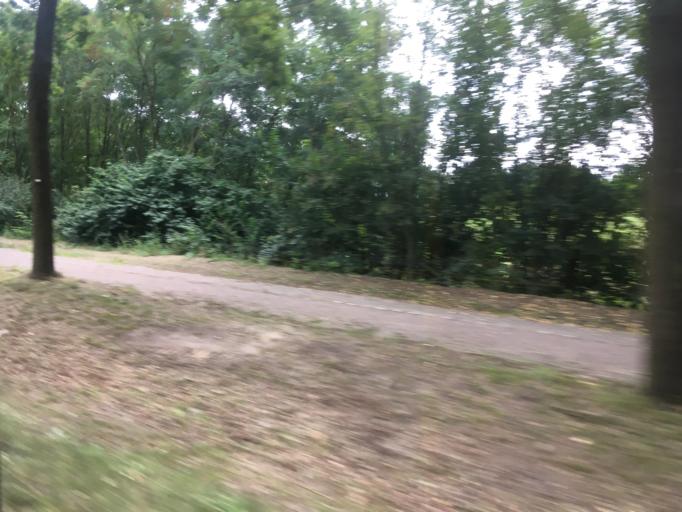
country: DE
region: Berlin
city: Wilhelmstadt
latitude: 52.5050
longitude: 13.1631
